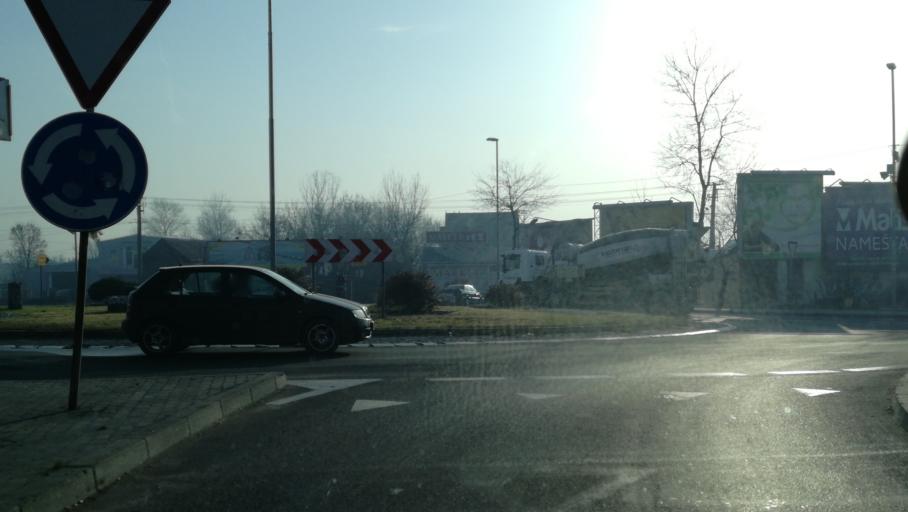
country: RS
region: Central Serbia
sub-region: Moravicki Okrug
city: Cacak
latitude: 43.8996
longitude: 20.3949
